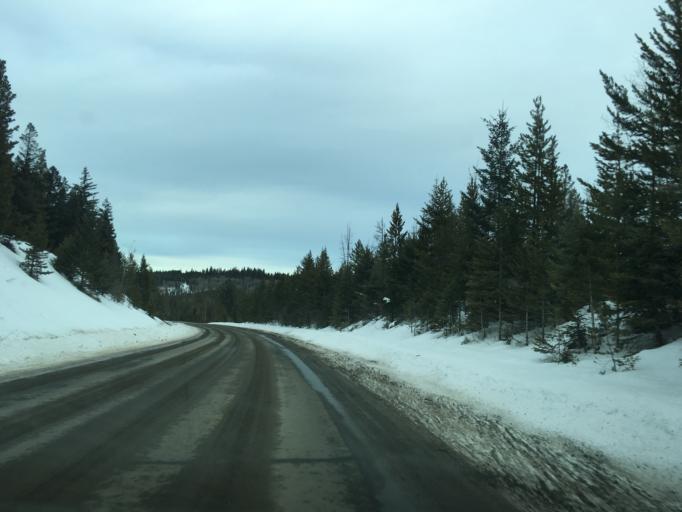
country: CA
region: British Columbia
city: Kamloops
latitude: 50.5275
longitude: -120.4567
